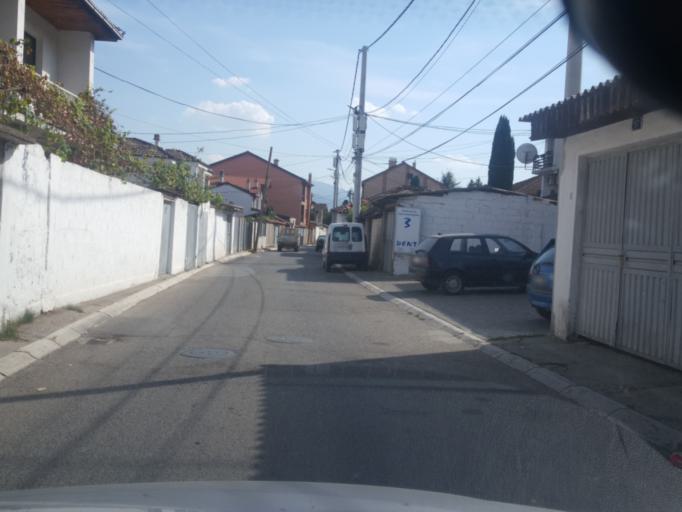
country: XK
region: Gjakova
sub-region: Komuna e Gjakoves
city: Gjakove
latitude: 42.3784
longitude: 20.4249
